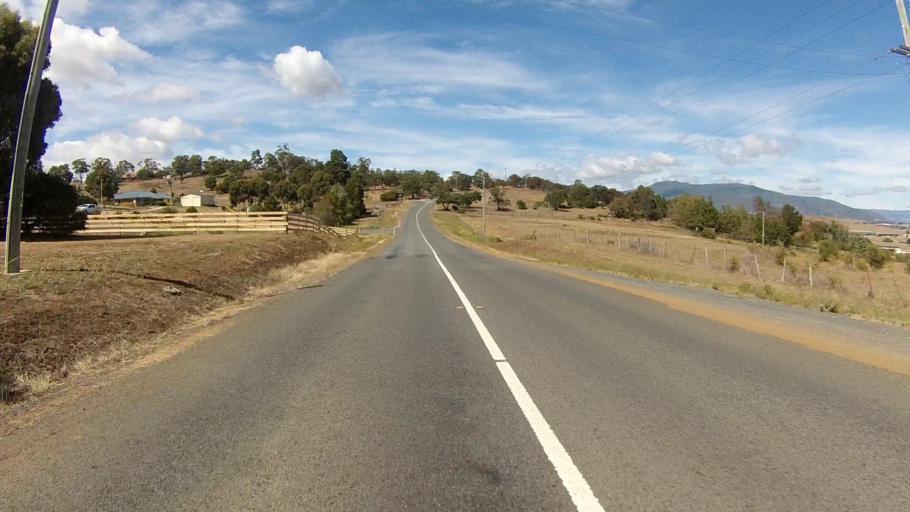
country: AU
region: Tasmania
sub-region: Brighton
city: Bridgewater
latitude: -42.7046
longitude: 147.2708
